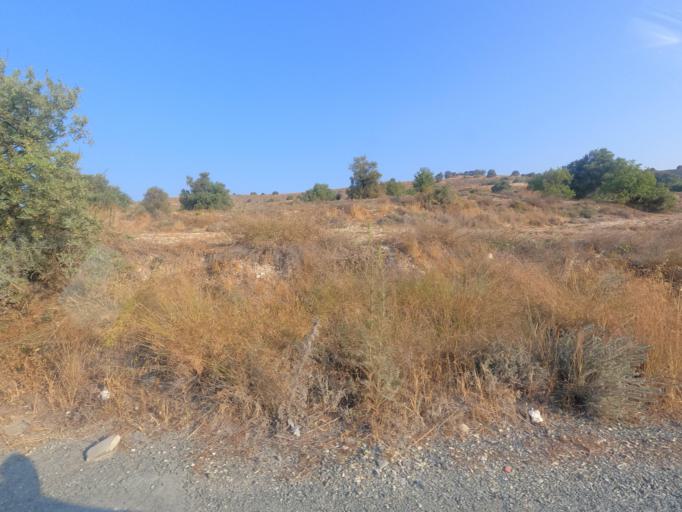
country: CY
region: Larnaka
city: Psevdas
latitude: 34.9358
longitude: 33.5018
